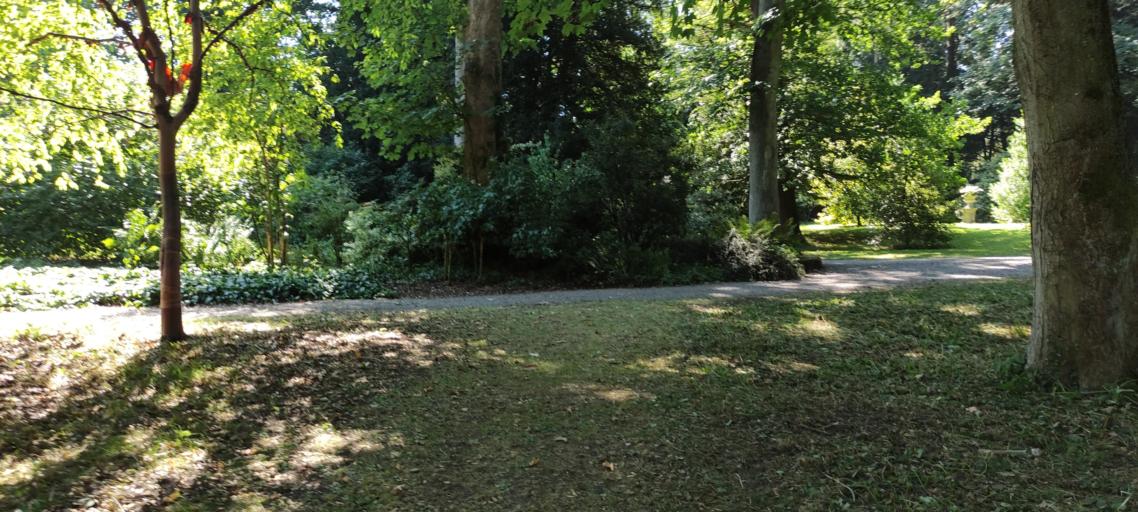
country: GB
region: England
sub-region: North Yorkshire
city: Bedale
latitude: 54.2662
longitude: -1.5998
